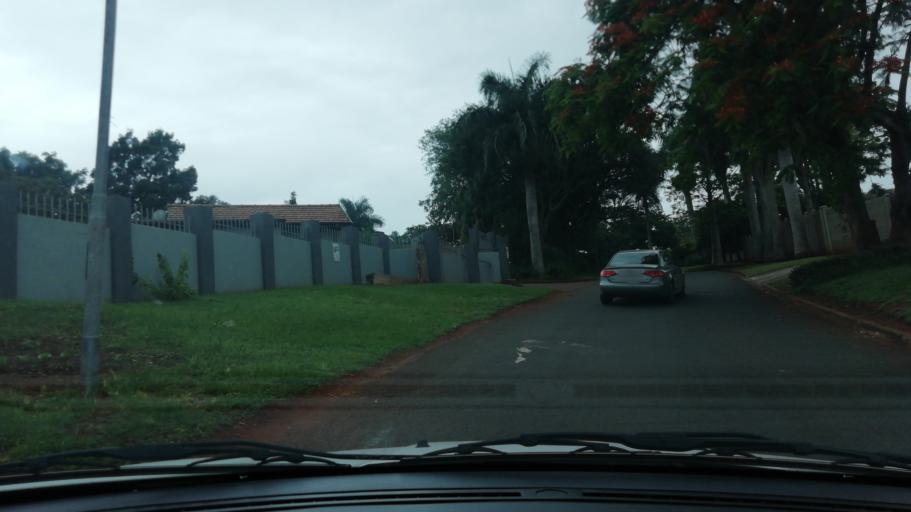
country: ZA
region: KwaZulu-Natal
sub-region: uThungulu District Municipality
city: Empangeni
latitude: -28.7601
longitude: 31.8925
